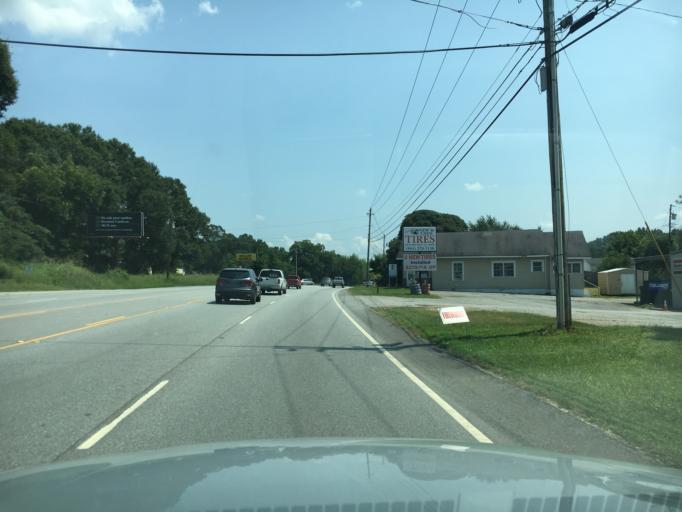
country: US
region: South Carolina
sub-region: Anderson County
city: Pendleton
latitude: 34.5975
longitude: -82.7522
